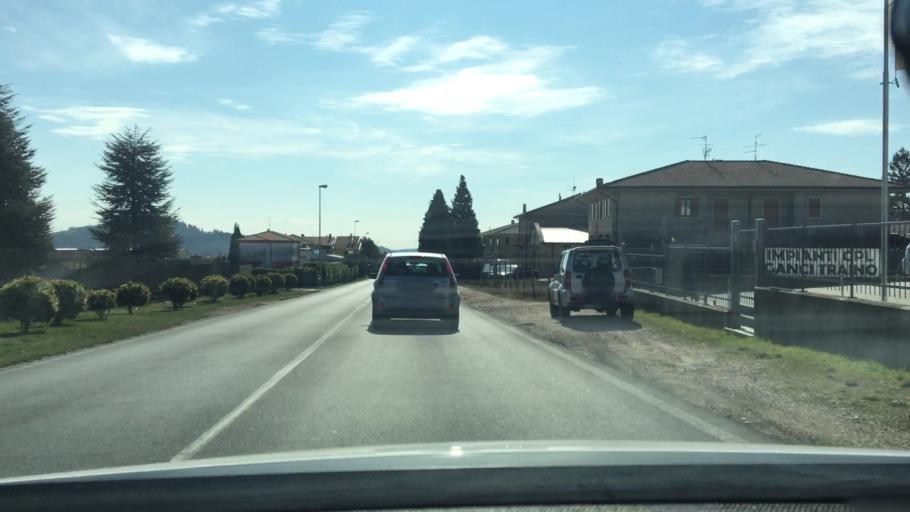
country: IT
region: Veneto
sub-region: Provincia di Verona
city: Cellore
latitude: 45.4902
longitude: 11.1753
